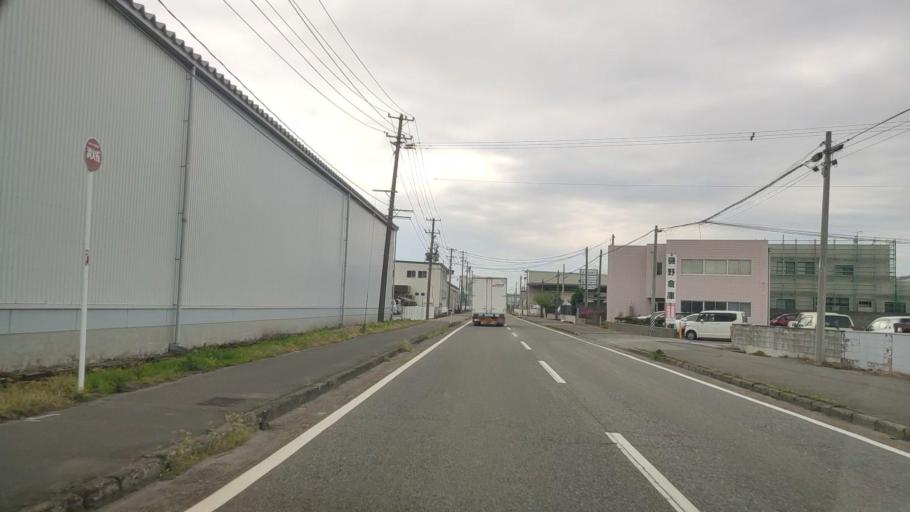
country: JP
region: Niigata
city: Niigata-shi
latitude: 37.9486
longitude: 139.0804
